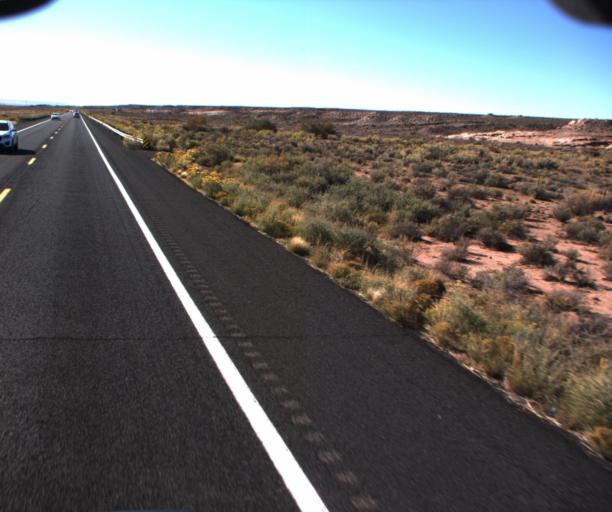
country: US
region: Arizona
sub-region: Coconino County
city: Tuba City
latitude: 36.1709
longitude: -111.3993
